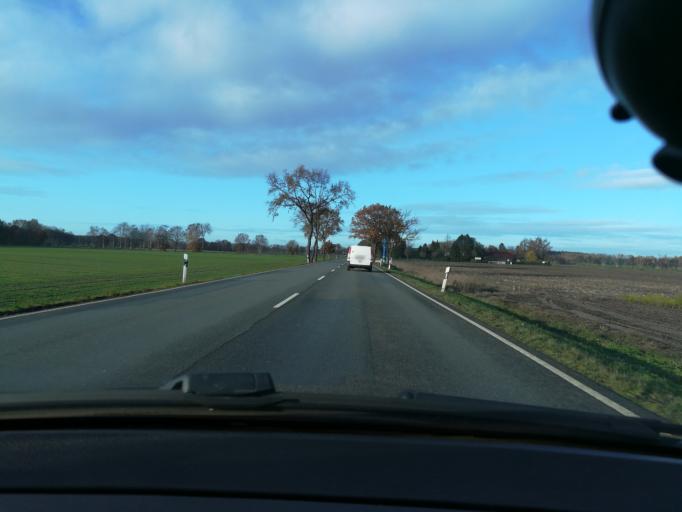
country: DE
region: Lower Saxony
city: Uchte
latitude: 52.5175
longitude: 8.8981
